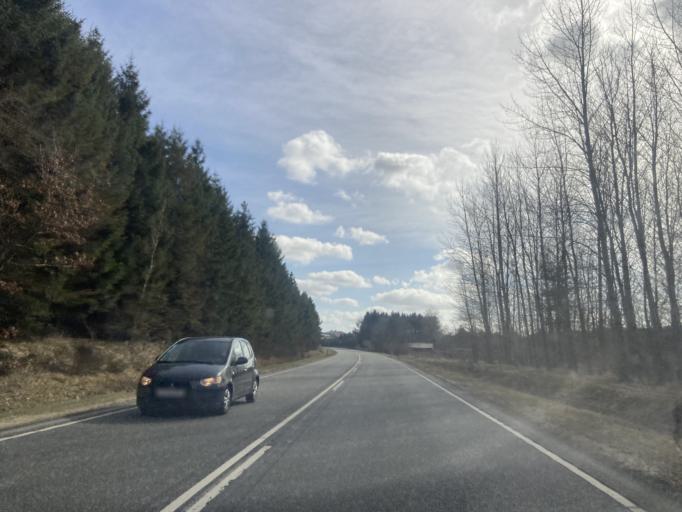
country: DK
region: Central Jutland
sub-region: Hedensted Kommune
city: Torring
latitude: 55.9779
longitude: 9.3942
